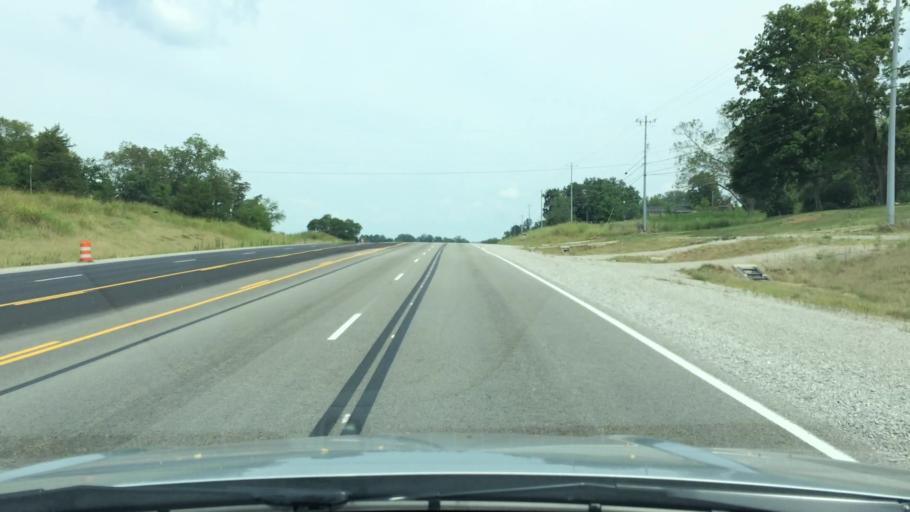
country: US
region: Tennessee
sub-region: Giles County
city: Pulaski
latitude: 35.1623
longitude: -87.0104
